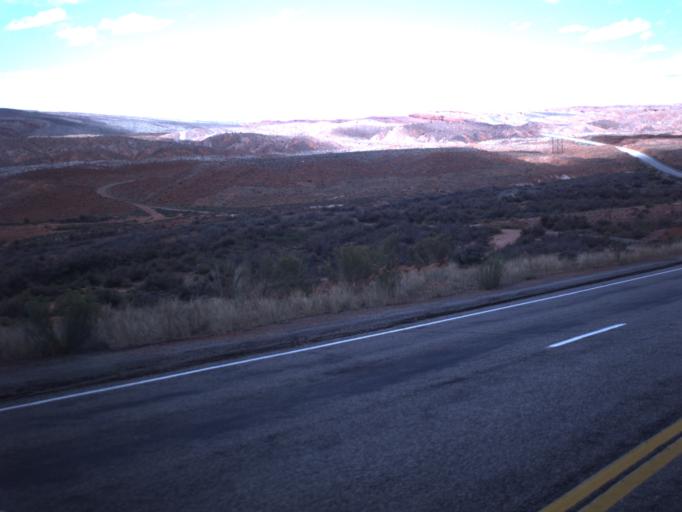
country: US
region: Utah
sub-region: San Juan County
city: Blanding
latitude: 37.2632
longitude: -109.6737
